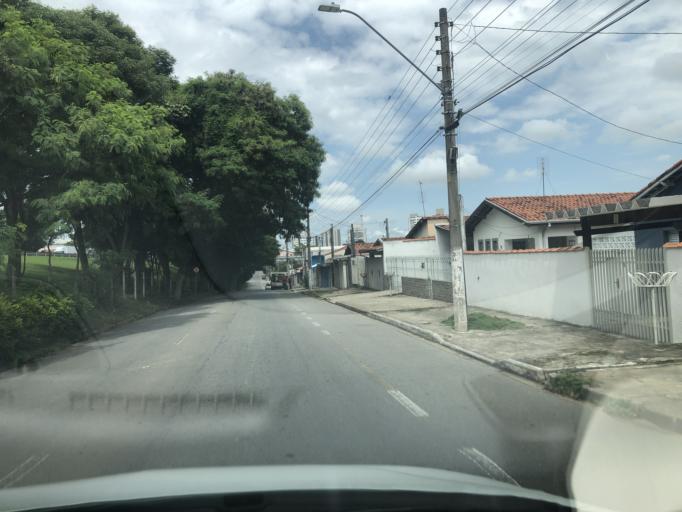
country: BR
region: Sao Paulo
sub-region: Taubate
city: Taubate
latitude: -23.0407
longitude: -45.5694
